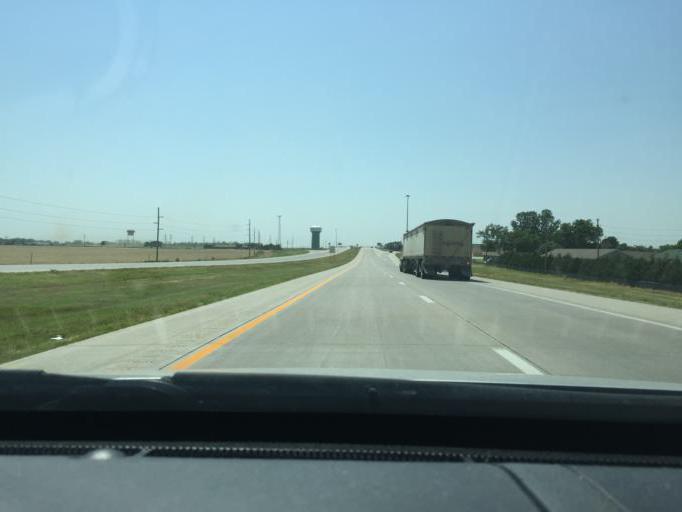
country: US
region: Kansas
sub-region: Reno County
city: South Hutchinson
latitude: 38.0133
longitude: -97.9334
